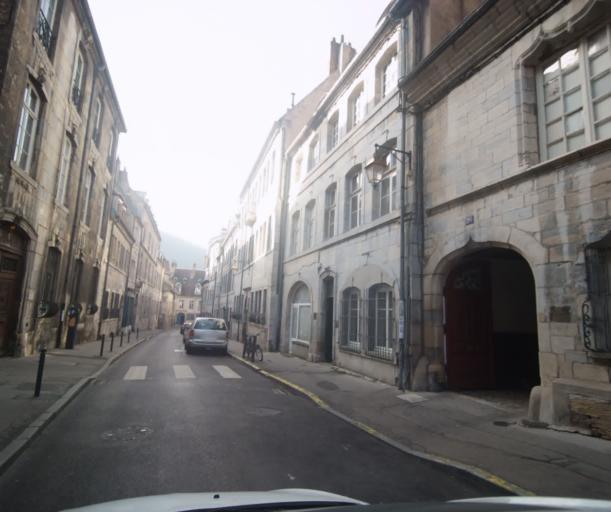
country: FR
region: Franche-Comte
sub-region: Departement du Doubs
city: Besancon
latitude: 47.2339
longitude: 6.0287
